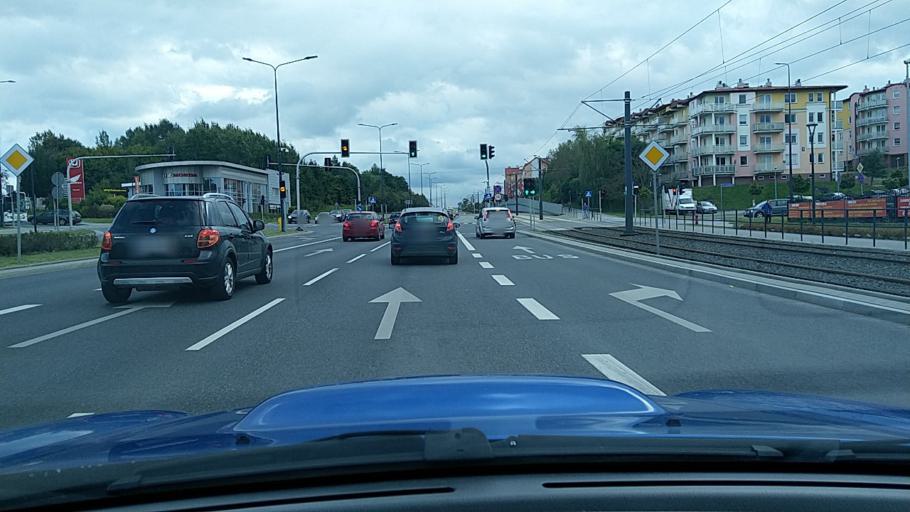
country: PL
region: Warmian-Masurian Voivodeship
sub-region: Olsztyn
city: Kortowo
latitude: 53.7477
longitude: 20.4870
